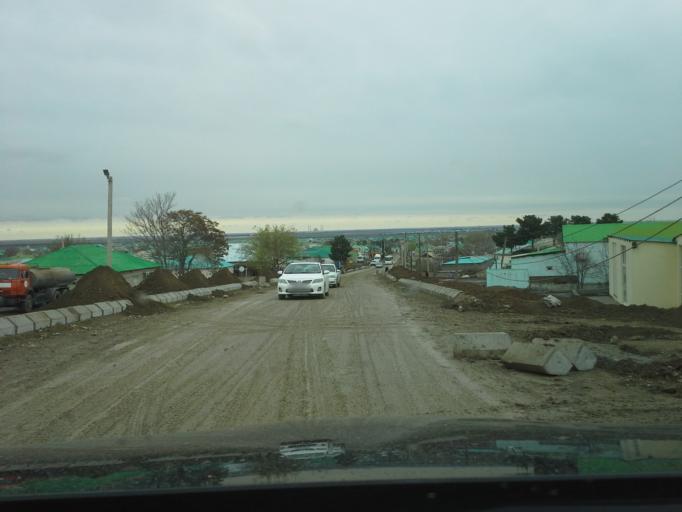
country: TM
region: Ahal
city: Abadan
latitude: 37.9620
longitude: 58.2116
